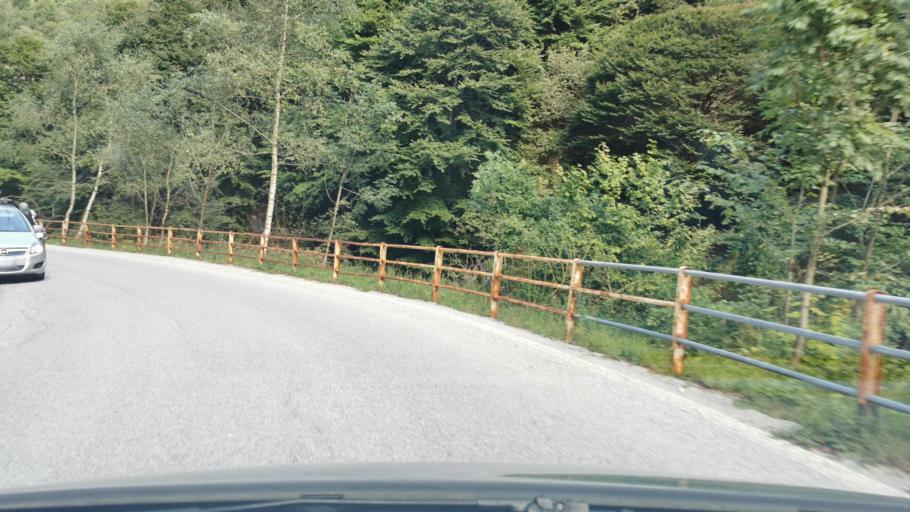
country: IT
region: Piedmont
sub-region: Provincia di Cuneo
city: Campomolino
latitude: 44.4112
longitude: 7.2382
